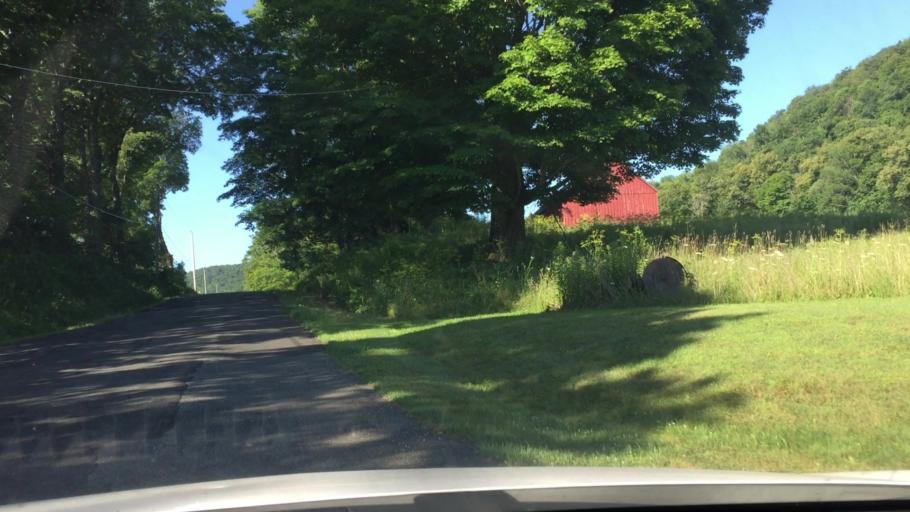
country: US
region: Massachusetts
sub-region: Berkshire County
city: Lee
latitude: 42.2441
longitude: -73.2045
